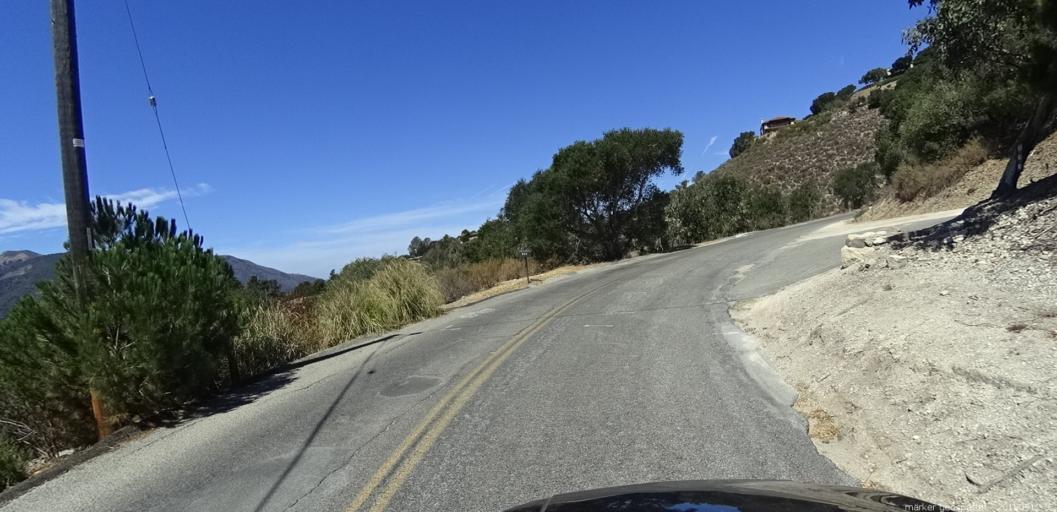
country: US
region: California
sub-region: Monterey County
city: Carmel Valley Village
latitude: 36.4863
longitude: -121.7295
